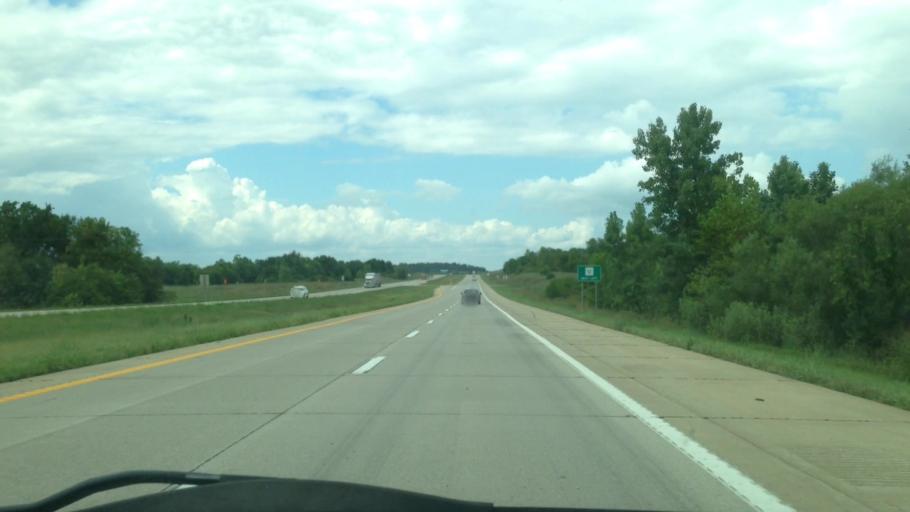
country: US
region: Missouri
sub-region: Pike County
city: Bowling Green
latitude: 39.4065
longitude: -91.2462
